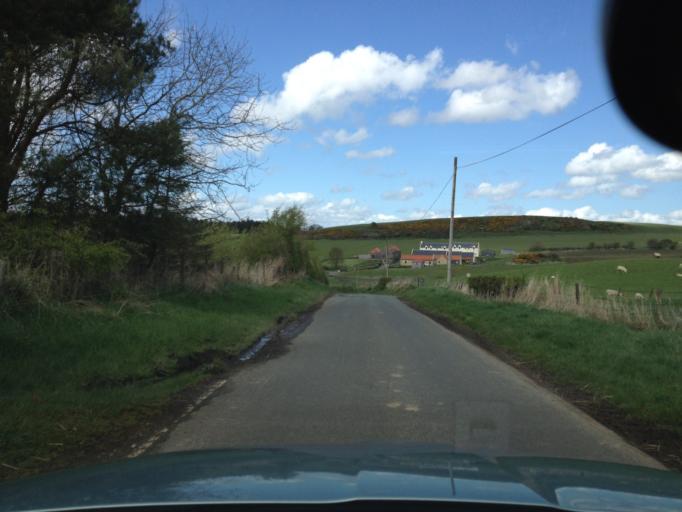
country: GB
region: Scotland
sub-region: West Lothian
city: Linlithgow
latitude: 55.9368
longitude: -3.5818
